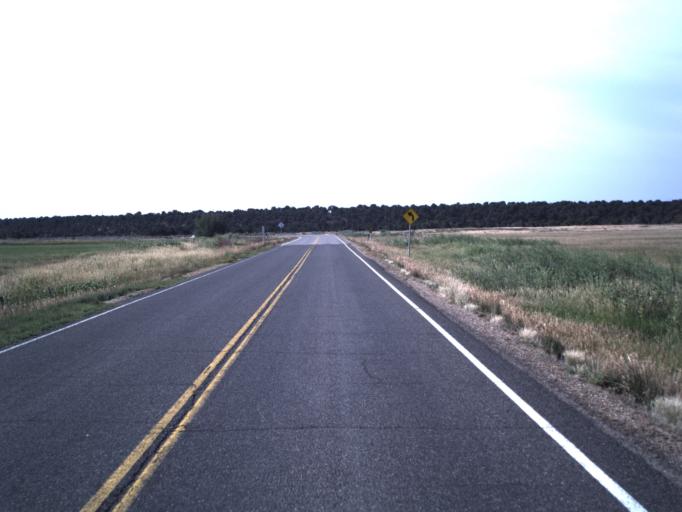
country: US
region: Utah
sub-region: Duchesne County
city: Duchesne
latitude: 40.3296
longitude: -110.4080
